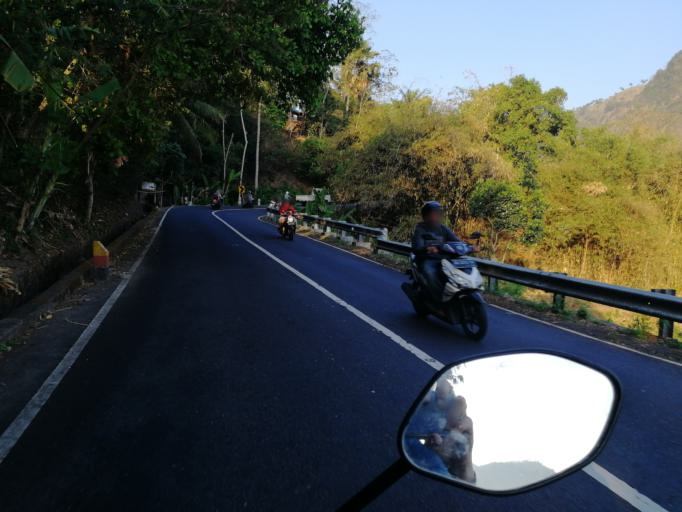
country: ID
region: Bali
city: Banjar Kangkaang
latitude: -8.3673
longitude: 115.6121
